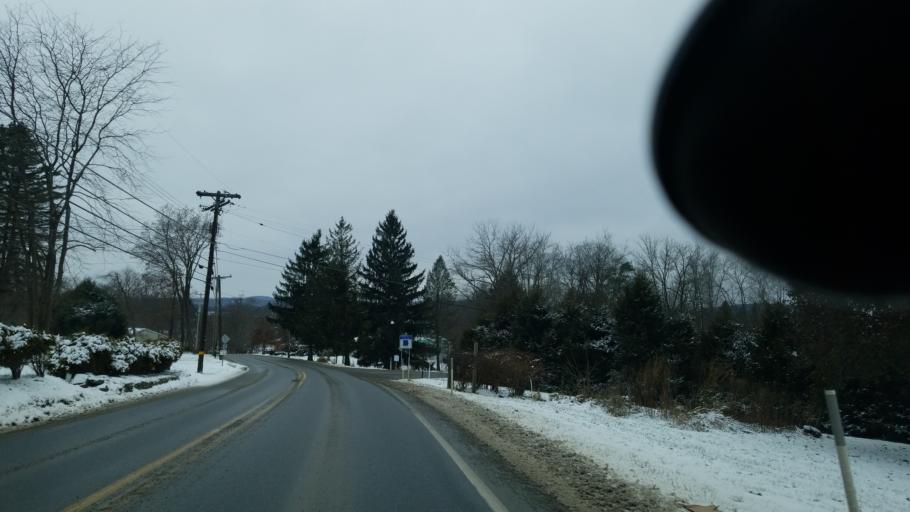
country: US
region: Pennsylvania
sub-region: Jefferson County
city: Albion
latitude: 40.9414
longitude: -78.9507
